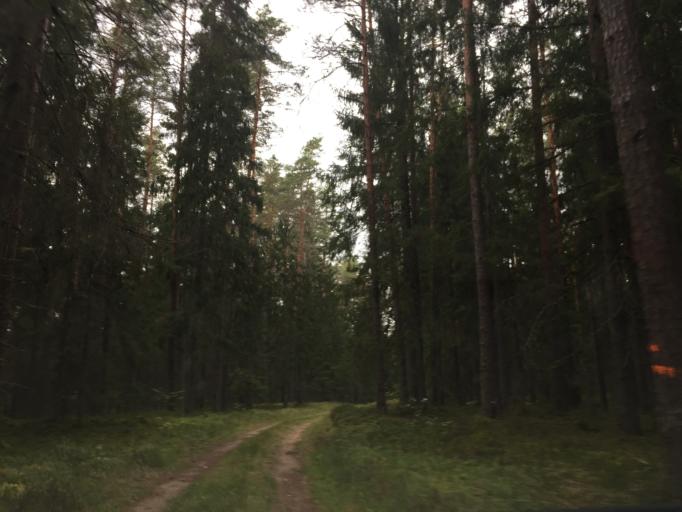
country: LV
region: Baldone
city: Baldone
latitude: 56.7731
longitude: 24.4500
